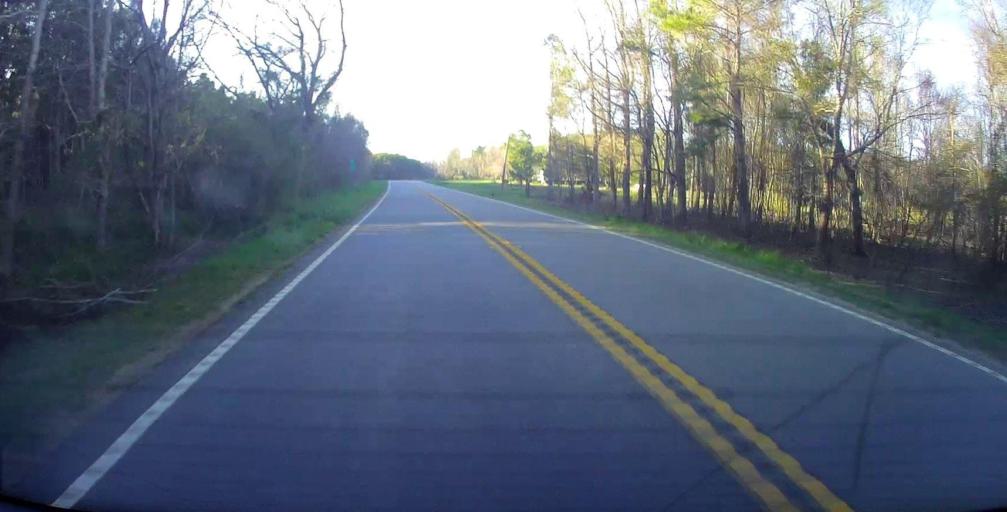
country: US
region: Georgia
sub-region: Pulaski County
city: Hawkinsville
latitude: 32.1814
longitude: -83.3626
